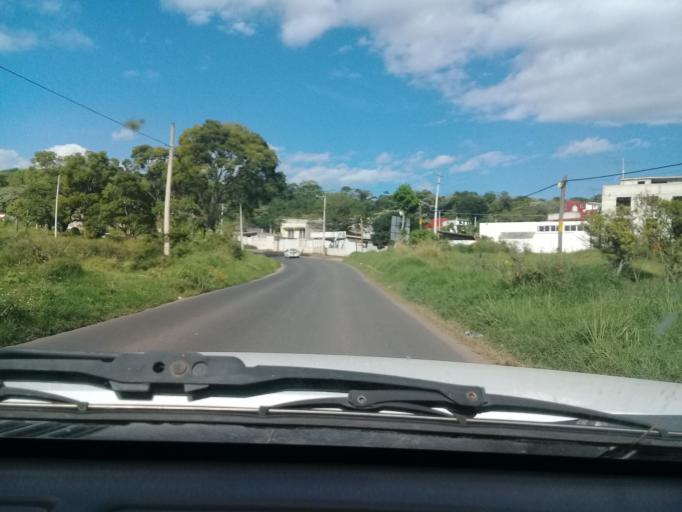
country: MX
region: Veracruz
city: El Castillo
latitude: 19.5485
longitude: -96.8781
